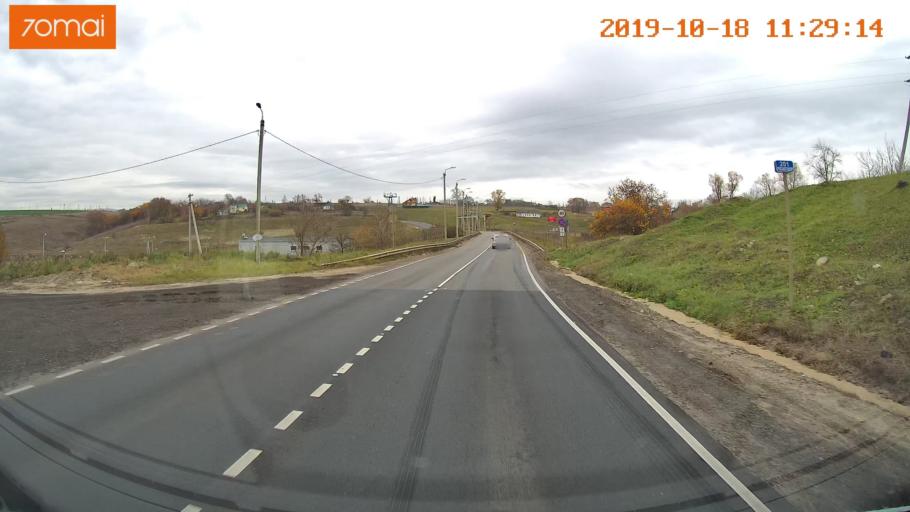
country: RU
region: Rjazan
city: Oktyabr'skiy
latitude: 54.1572
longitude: 38.6744
